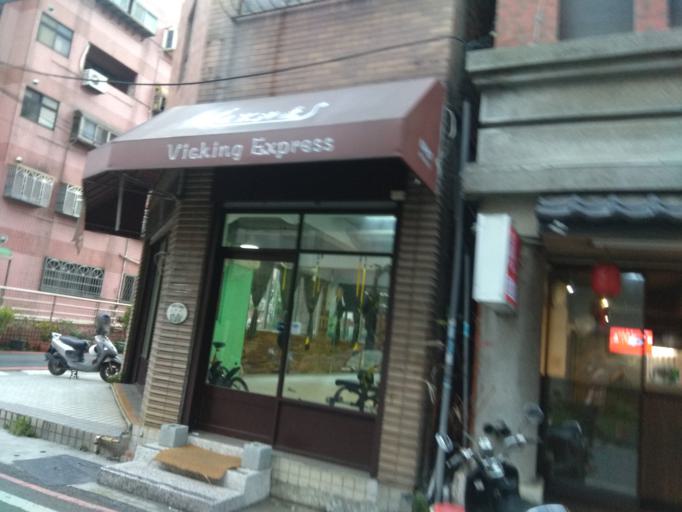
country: TW
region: Taiwan
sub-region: Taoyuan
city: Taoyuan
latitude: 24.9960
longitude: 121.3174
